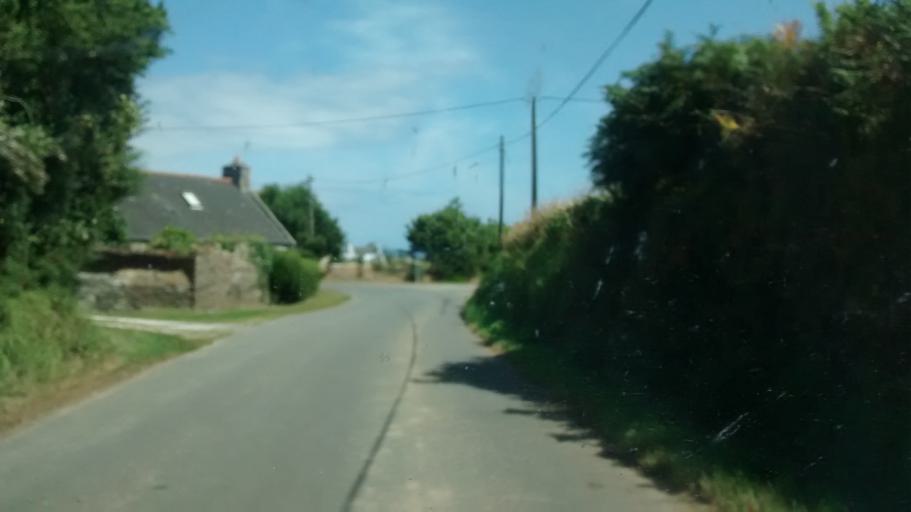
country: FR
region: Brittany
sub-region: Departement du Finistere
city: Plouguerneau
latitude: 48.6175
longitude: -4.4792
